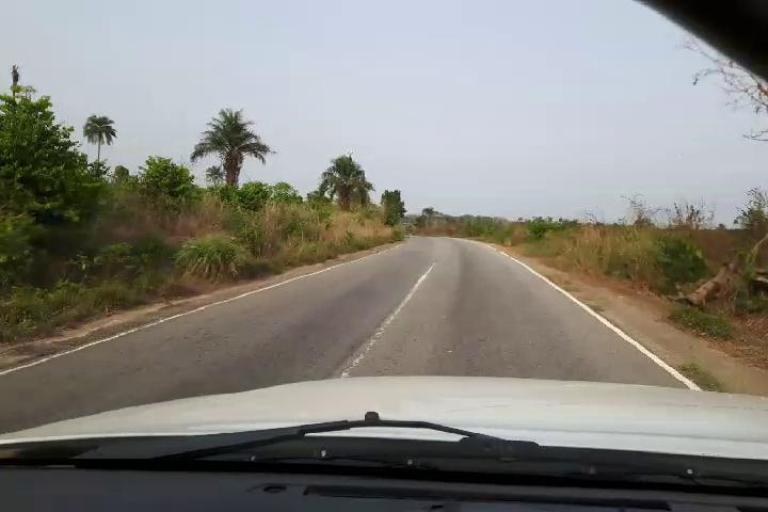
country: SL
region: Southern Province
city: Baoma
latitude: 7.9271
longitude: -11.5847
